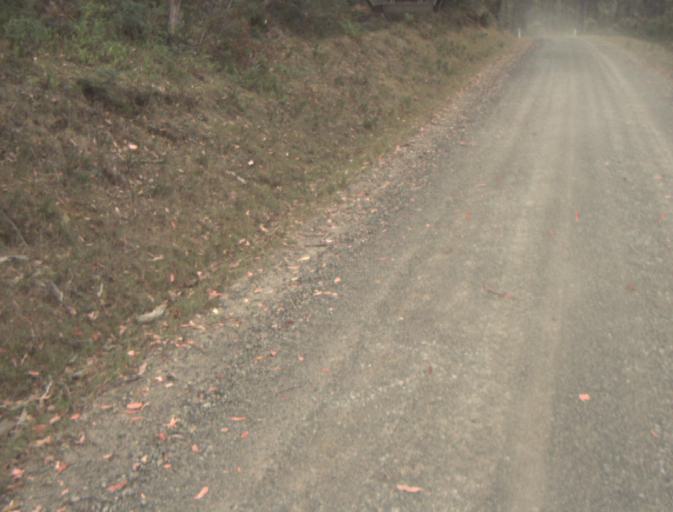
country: AU
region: Tasmania
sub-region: Dorset
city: Scottsdale
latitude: -41.4083
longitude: 147.5186
